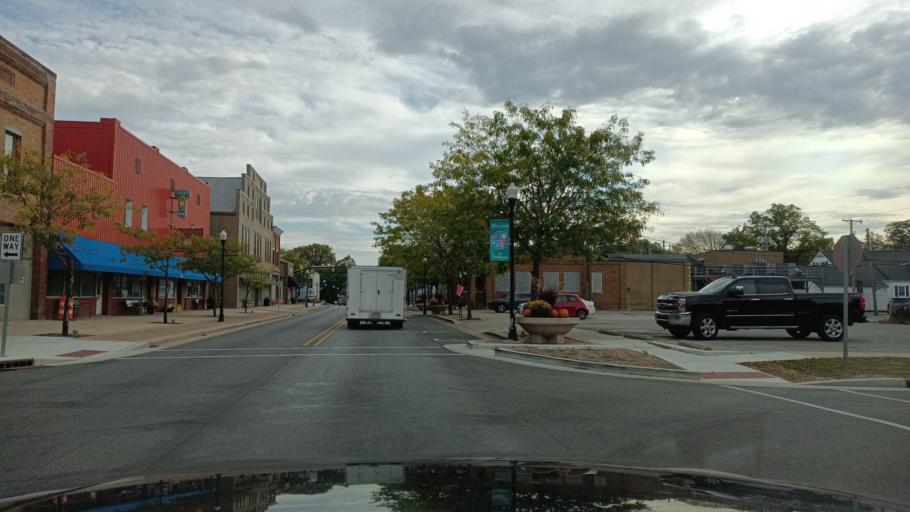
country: US
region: Indiana
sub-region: Delaware County
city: Yorktown
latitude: 40.1733
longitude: -85.4951
